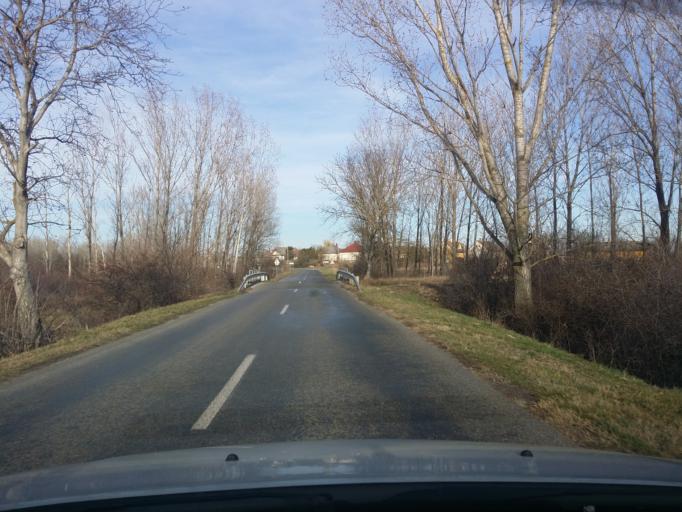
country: HU
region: Tolna
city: Madocsa
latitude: 46.6791
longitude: 18.9397
